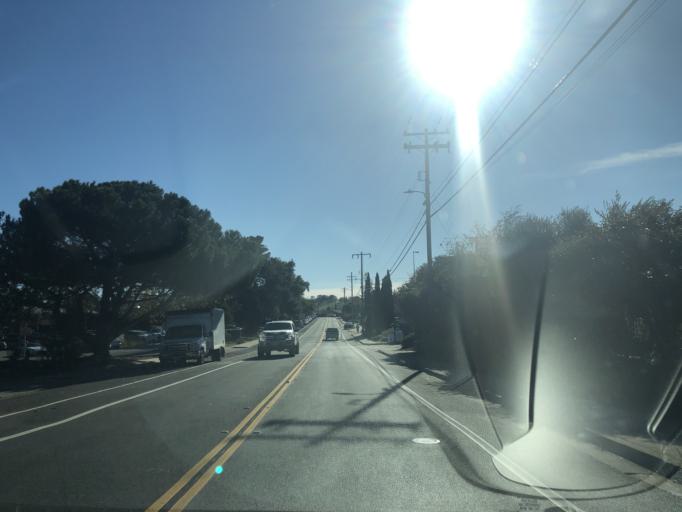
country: US
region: California
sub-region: Contra Costa County
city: Pacheco
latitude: 37.9896
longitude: -122.0874
